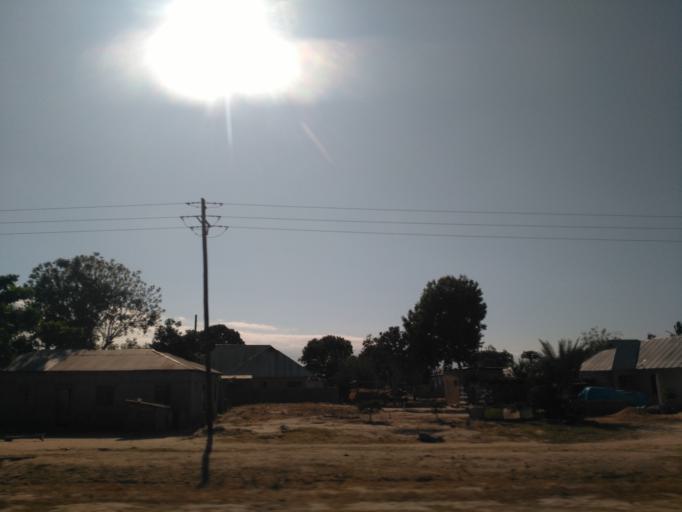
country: TZ
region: Dodoma
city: Dodoma
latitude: -6.1038
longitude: 35.7481
